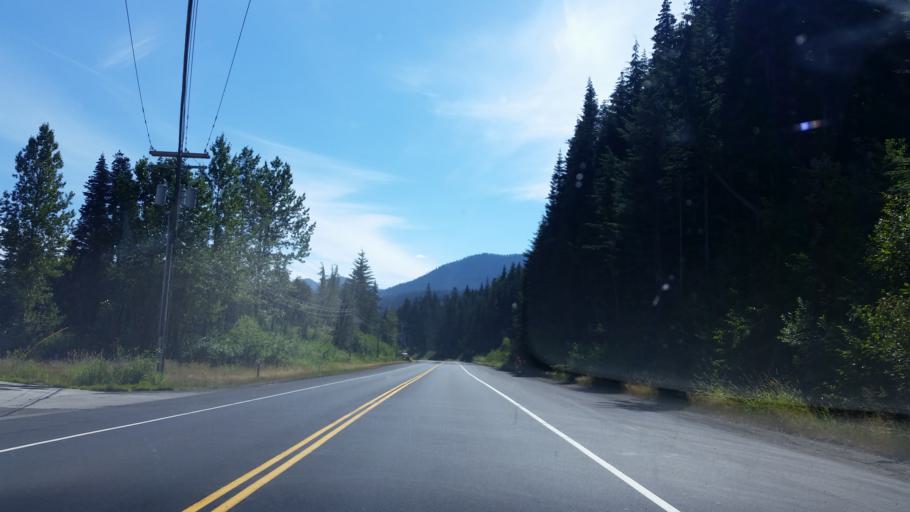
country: US
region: Washington
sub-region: King County
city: Tanner
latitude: 47.4172
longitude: -121.4131
